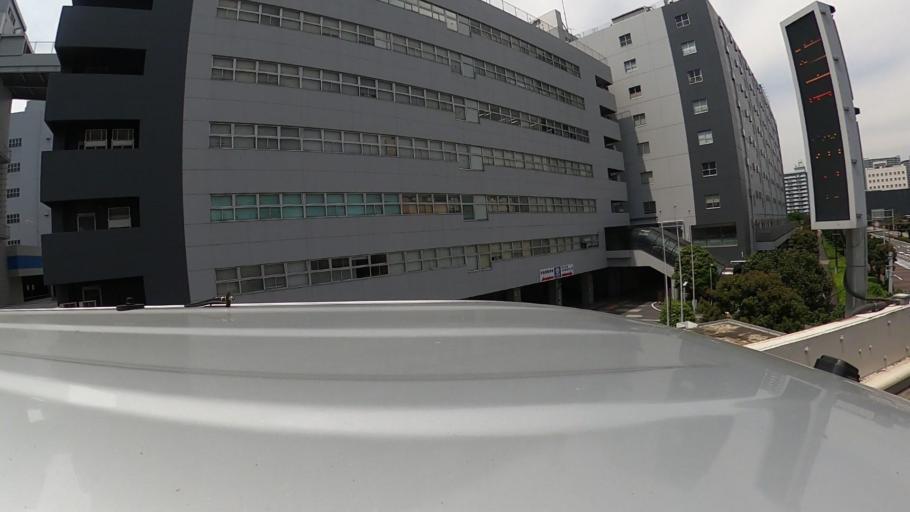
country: JP
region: Kanagawa
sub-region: Kawasaki-shi
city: Kawasaki
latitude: 35.6006
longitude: 139.7452
